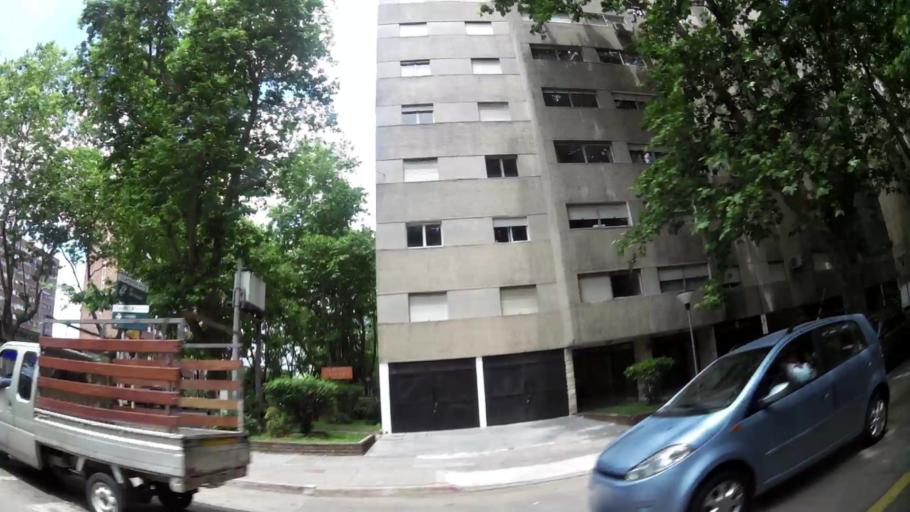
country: UY
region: Montevideo
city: Montevideo
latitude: -34.8904
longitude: -56.1933
